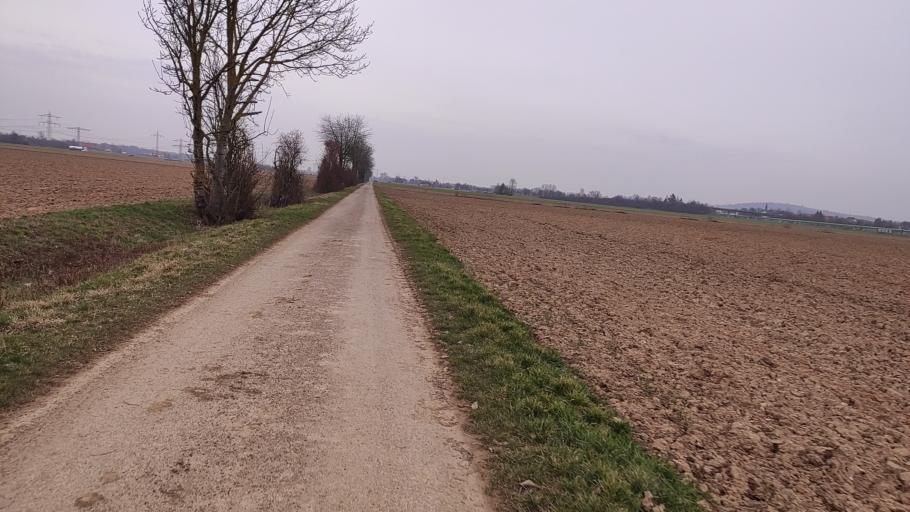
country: DE
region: Baden-Wuerttemberg
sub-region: Freiburg Region
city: Kenzingen
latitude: 48.1796
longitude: 7.7597
